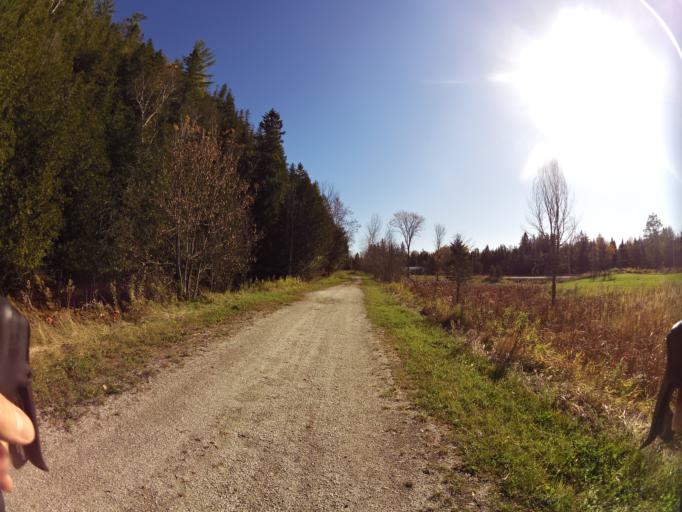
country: CA
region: Quebec
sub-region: Outaouais
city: Wakefield
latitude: 45.8479
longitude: -75.9864
